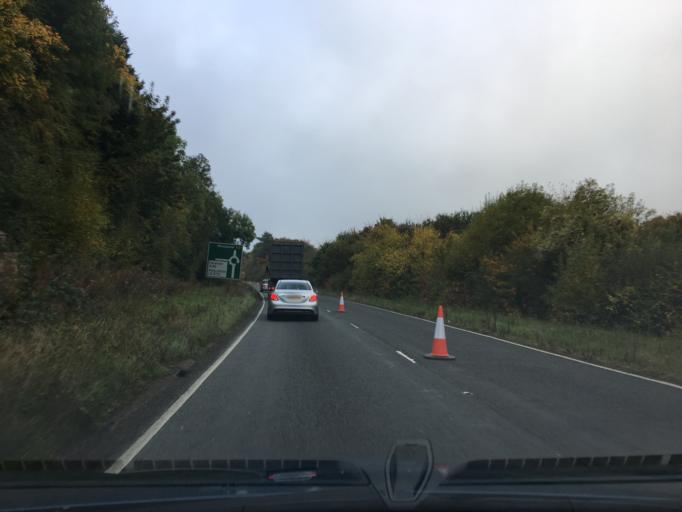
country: GB
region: England
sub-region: Hampshire
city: Alton
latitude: 51.1353
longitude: -0.9903
